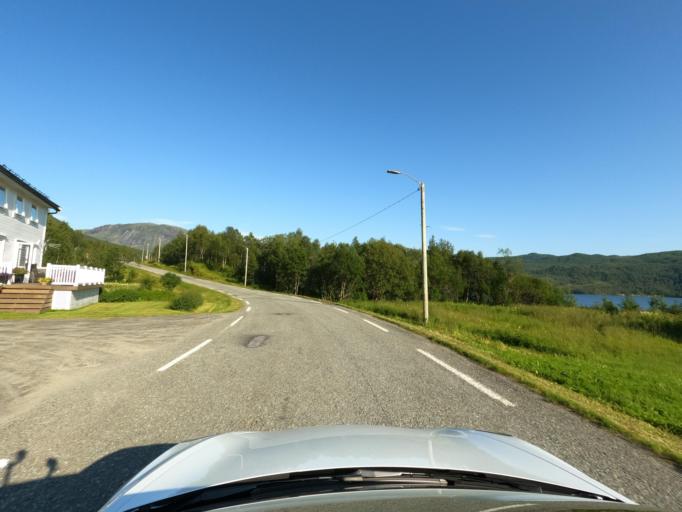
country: NO
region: Troms
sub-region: Gratangen
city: Gratangen
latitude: 68.5612
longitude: 17.6902
